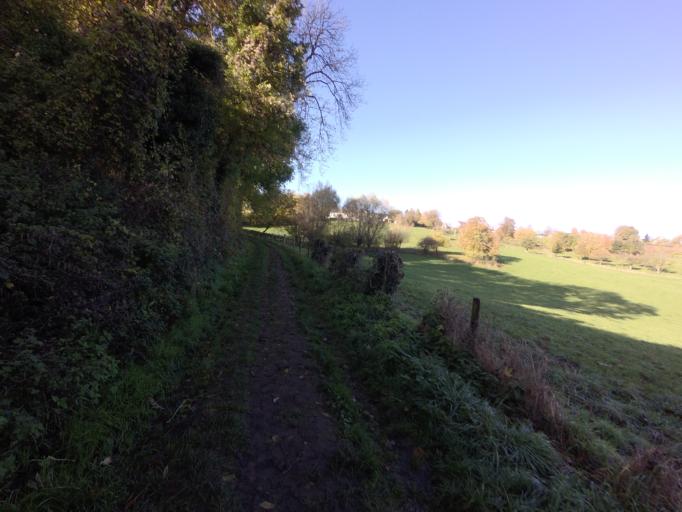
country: NL
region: Limburg
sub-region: Gemeente Voerendaal
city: Ubachsberg
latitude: 50.8363
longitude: 5.9349
